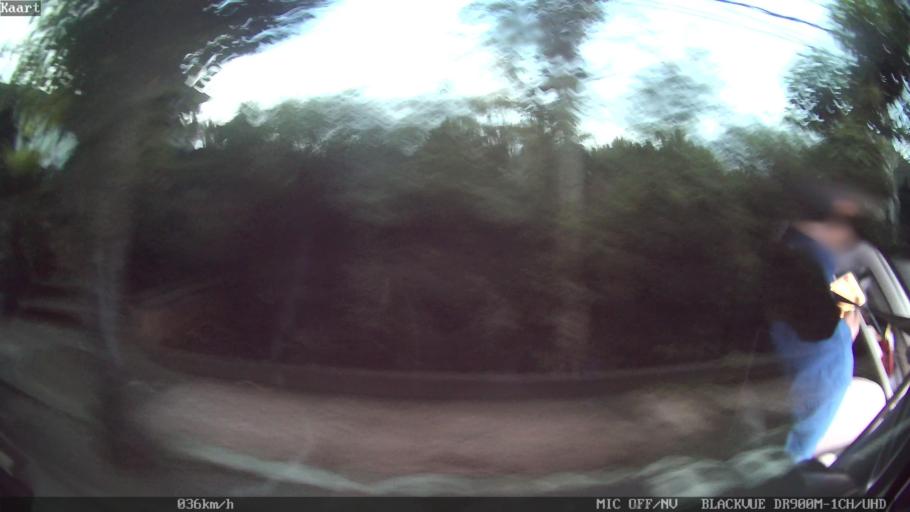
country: ID
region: Bali
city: Bunutan
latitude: -8.4809
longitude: 115.2472
